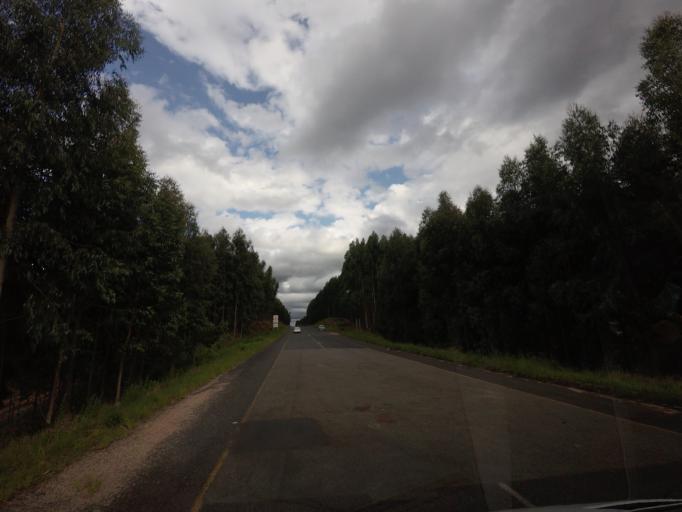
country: ZA
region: Mpumalanga
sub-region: Ehlanzeni District
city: Graksop
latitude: -24.9908
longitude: 30.9928
